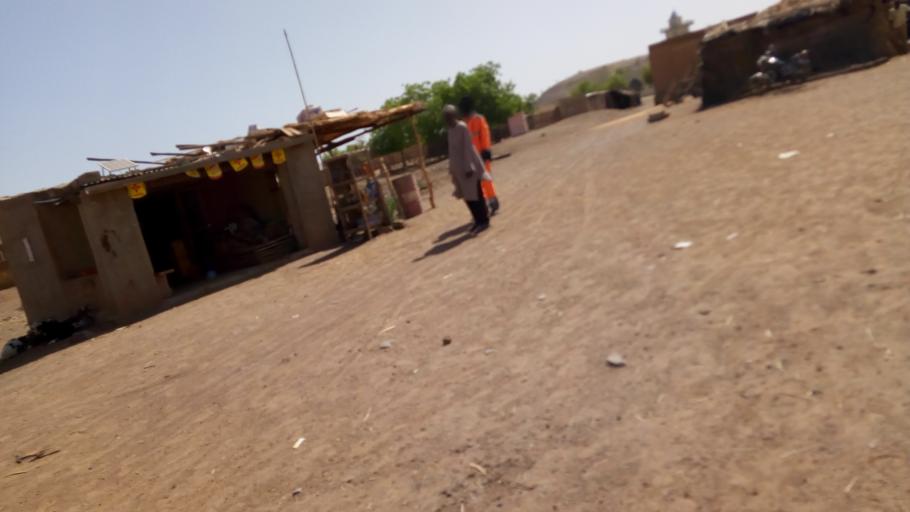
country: ML
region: Kayes
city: Yelimane
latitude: 14.6425
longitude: -10.6996
